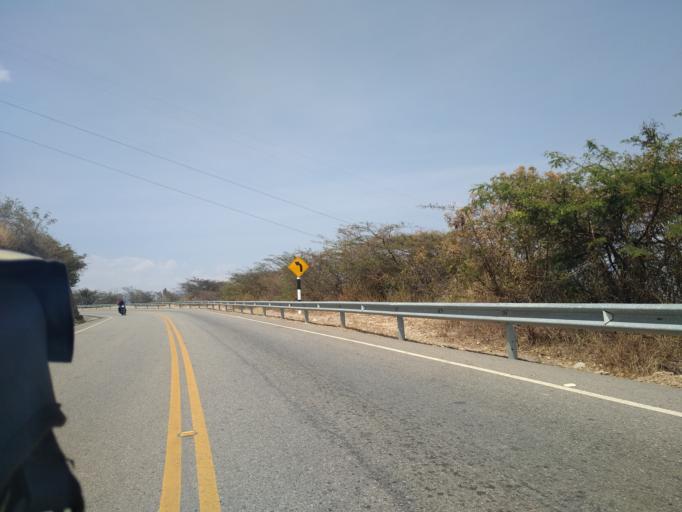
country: PE
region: Cajamarca
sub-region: Provincia de Cajabamba
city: Cauday
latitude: -7.6124
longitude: -78.0862
